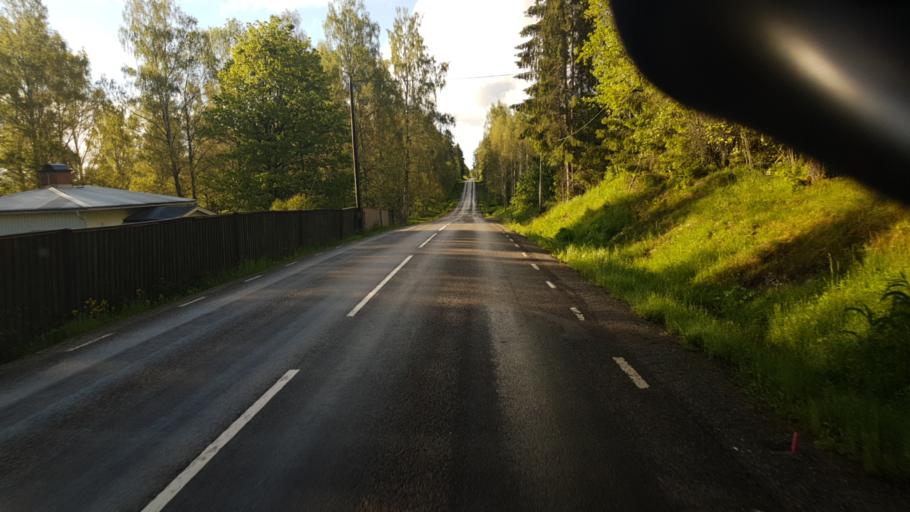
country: SE
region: Vaermland
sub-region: Arvika Kommun
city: Arvika
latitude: 59.6295
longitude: 12.4954
